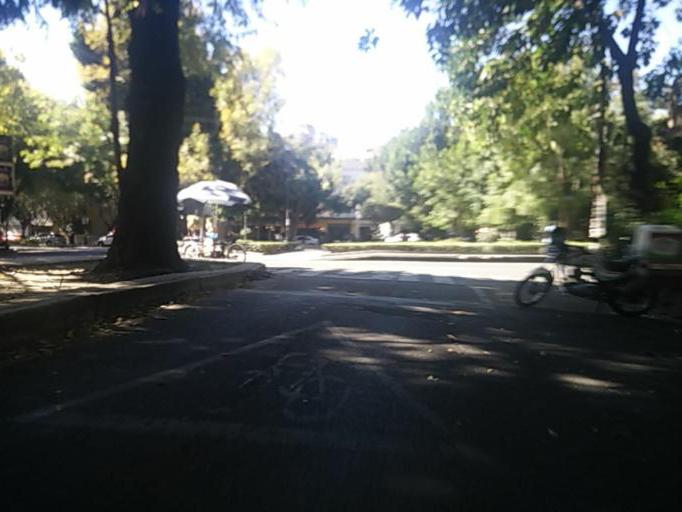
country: MX
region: Mexico City
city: Benito Juarez
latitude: 19.4095
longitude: -99.1708
